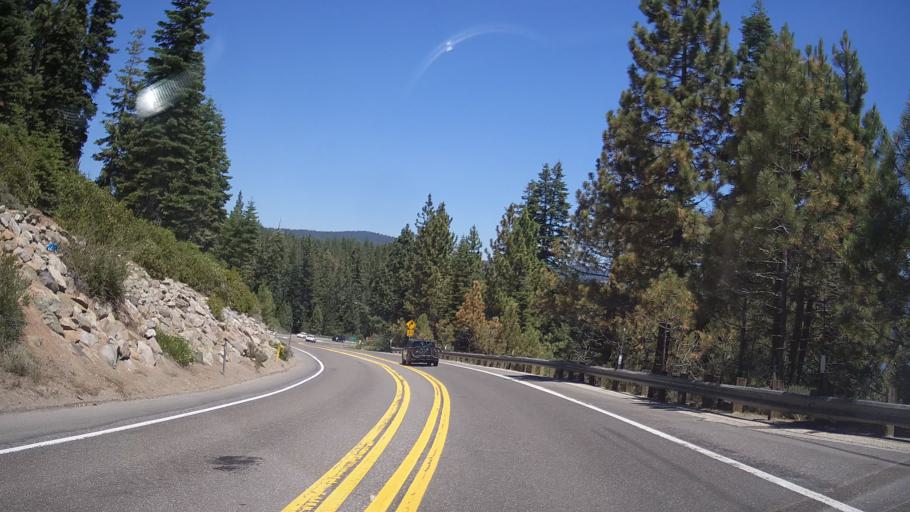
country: US
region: California
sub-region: Placer County
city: Dollar Point
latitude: 39.1957
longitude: -120.0994
